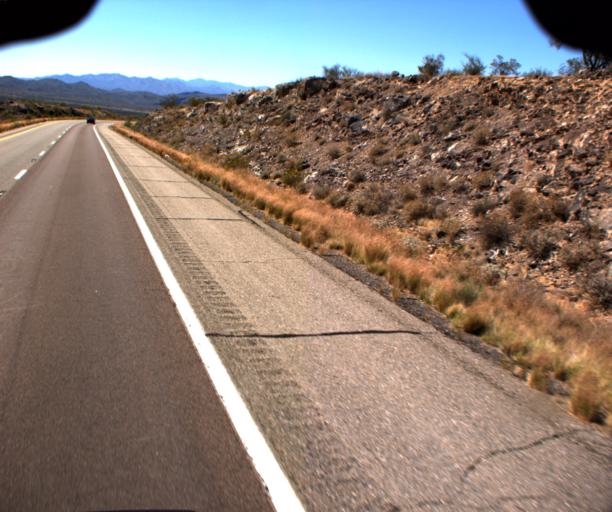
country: US
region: Arizona
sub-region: Yavapai County
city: Bagdad
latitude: 34.4936
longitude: -113.3907
